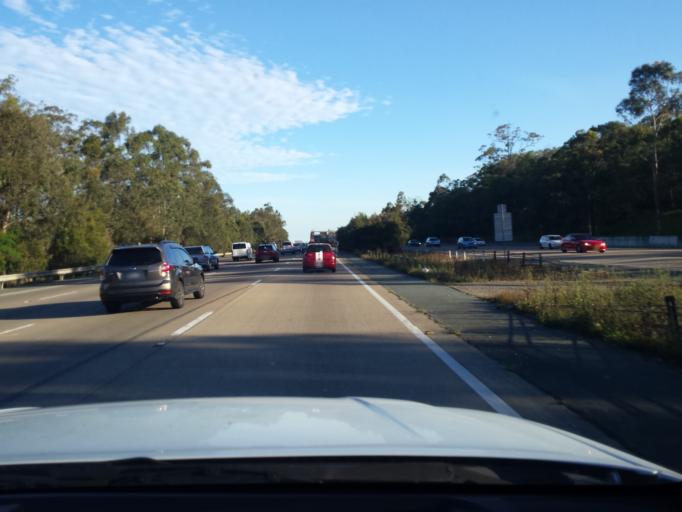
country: AU
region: Queensland
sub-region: Gold Coast
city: Oxenford
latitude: -27.8378
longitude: 153.3031
